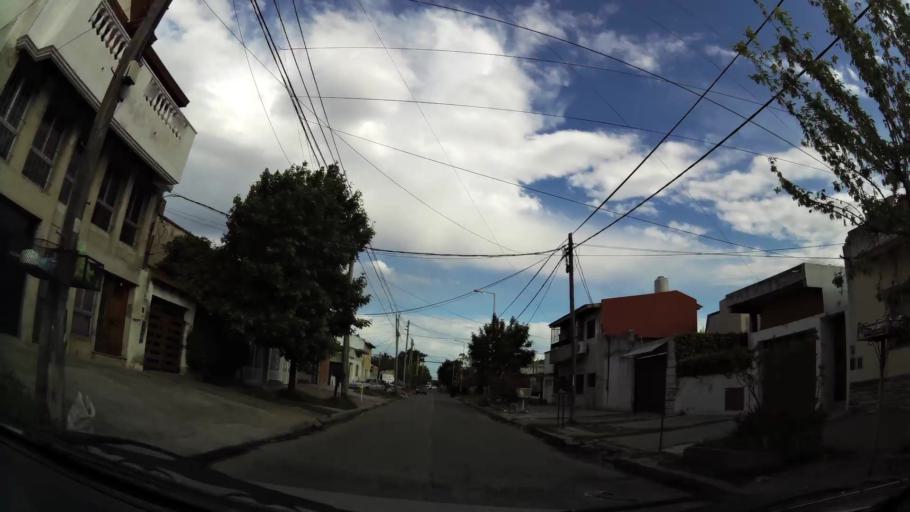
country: AR
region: Buenos Aires
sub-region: Partido de Avellaneda
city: Avellaneda
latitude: -34.6901
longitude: -58.3650
